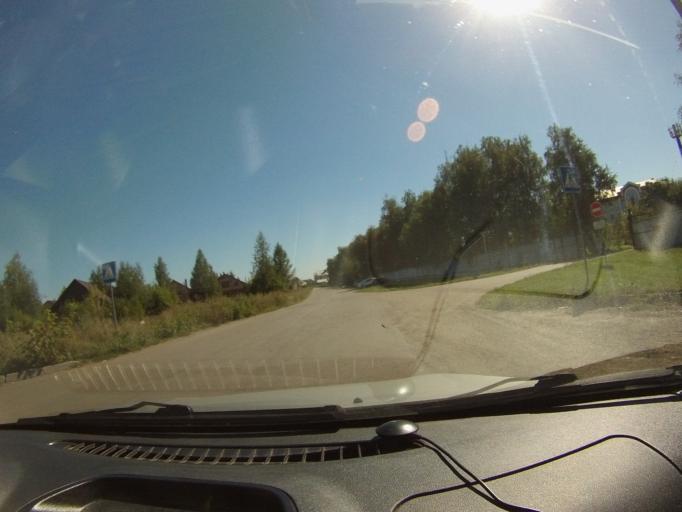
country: RU
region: Tambov
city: Komsomolets
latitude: 52.7679
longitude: 41.3616
